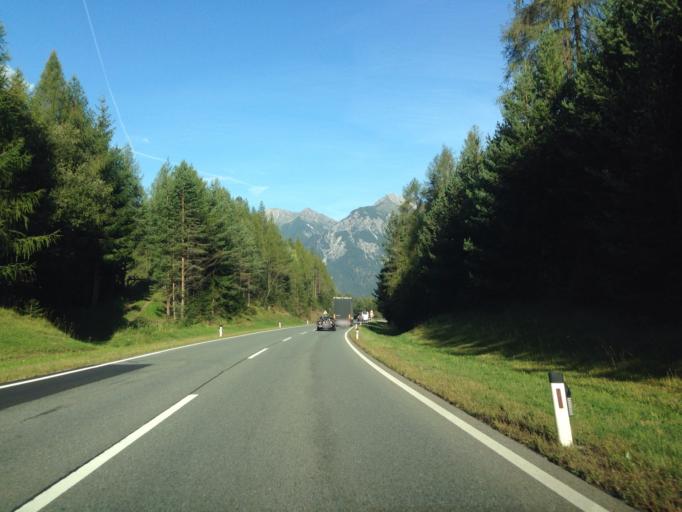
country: AT
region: Tyrol
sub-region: Politischer Bezirk Imst
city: Nassereith
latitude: 47.3064
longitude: 10.8663
